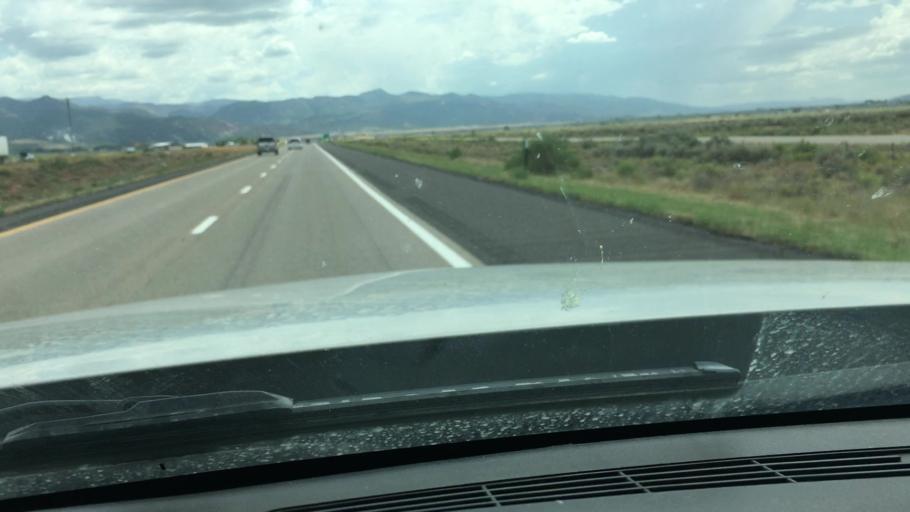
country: US
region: Utah
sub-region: Iron County
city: Parowan
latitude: 37.9238
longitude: -112.7695
